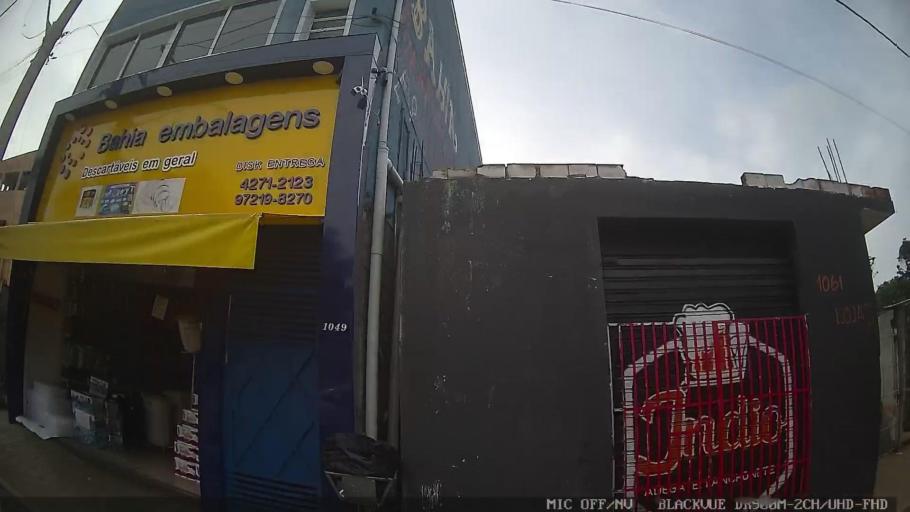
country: BR
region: Sao Paulo
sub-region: Poa
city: Poa
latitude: -23.5181
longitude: -46.3477
